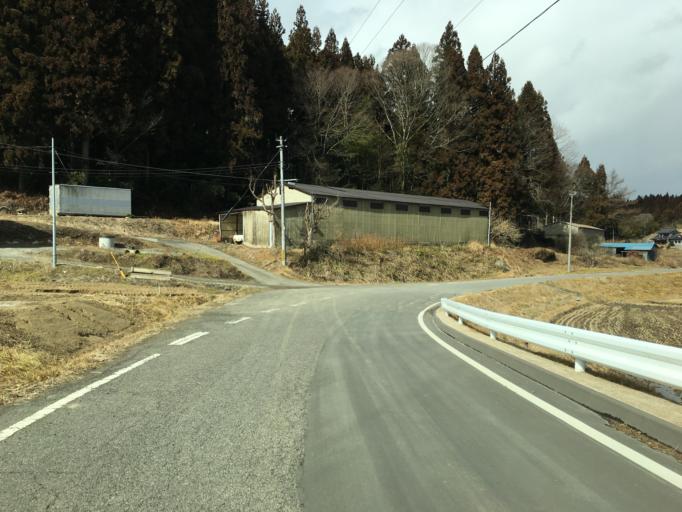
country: JP
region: Fukushima
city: Ishikawa
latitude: 37.2104
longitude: 140.5570
